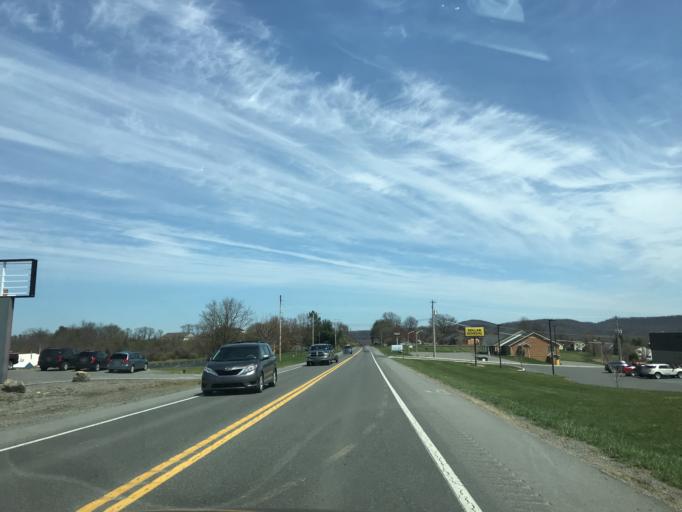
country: US
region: Pennsylvania
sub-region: Snyder County
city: Selinsgrove
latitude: 40.8072
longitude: -76.8790
